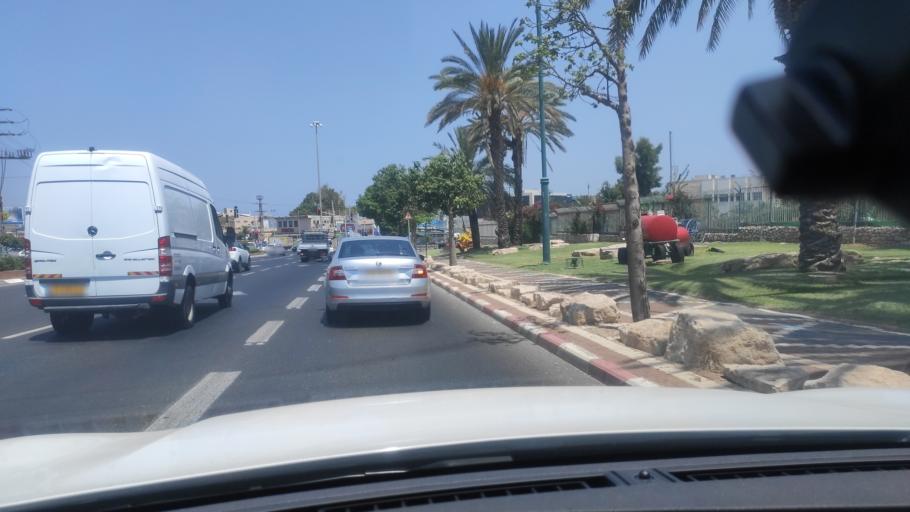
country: IL
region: Central District
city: Petah Tiqwa
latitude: 32.1011
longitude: 34.8987
